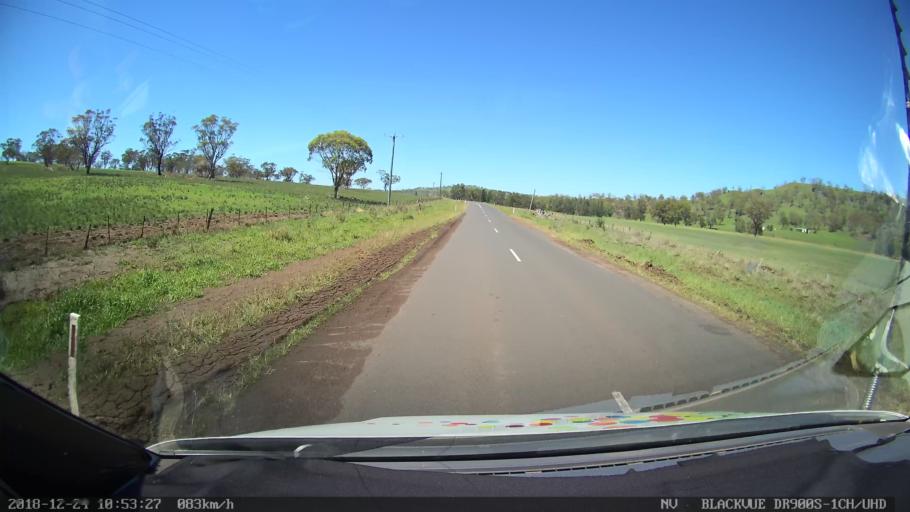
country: AU
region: New South Wales
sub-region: Upper Hunter Shire
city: Merriwa
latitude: -31.9917
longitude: 150.4209
